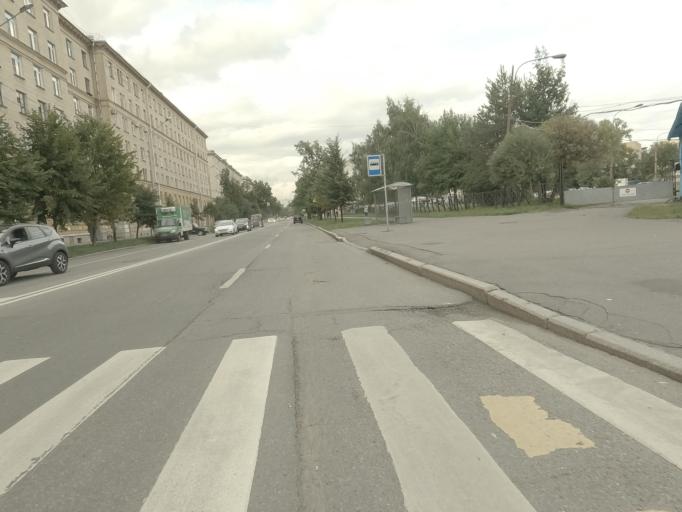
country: RU
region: St.-Petersburg
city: Avtovo
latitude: 59.8656
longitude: 30.2638
